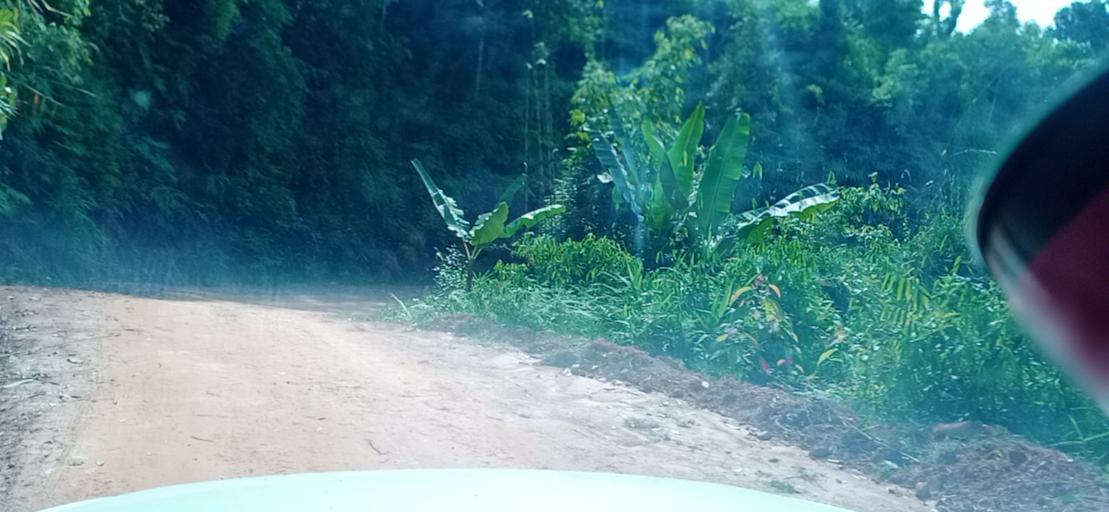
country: TH
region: Changwat Bueng Kan
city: Pak Khat
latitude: 18.6351
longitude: 103.2603
